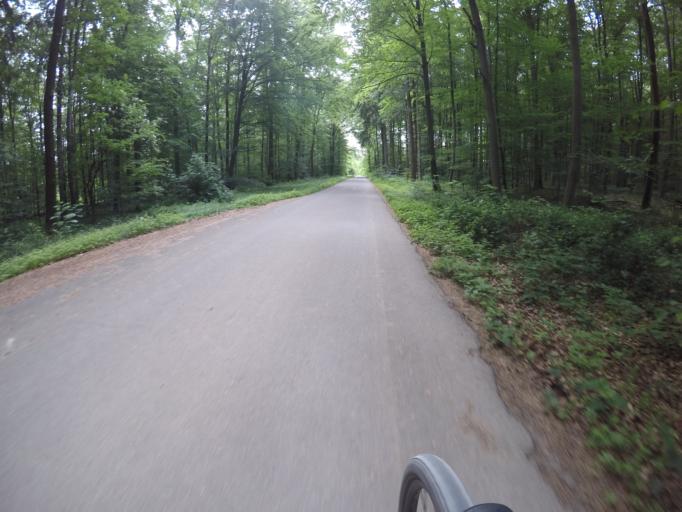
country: DE
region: Baden-Wuerttemberg
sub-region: Regierungsbezirk Stuttgart
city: Wendlingen am Neckar
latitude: 48.6496
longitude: 9.3958
